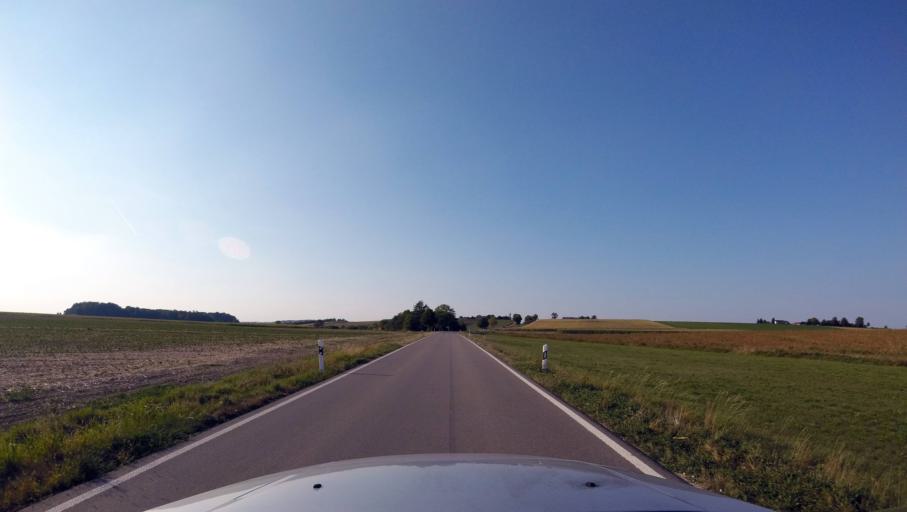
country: DE
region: Baden-Wuerttemberg
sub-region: Regierungsbezirk Stuttgart
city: Leutenbach
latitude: 48.9134
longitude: 9.4005
